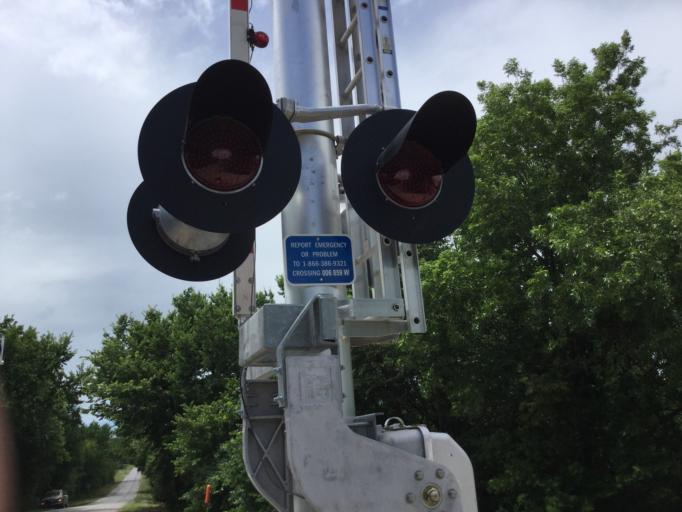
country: US
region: Kansas
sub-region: Montgomery County
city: Independence
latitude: 37.2220
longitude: -95.7368
